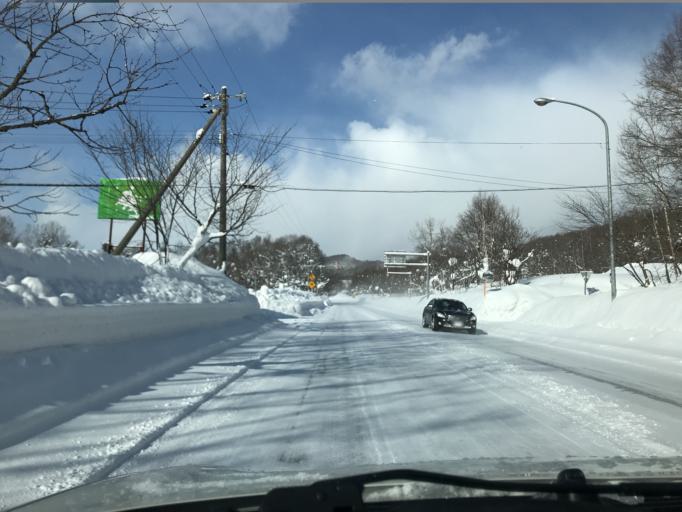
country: JP
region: Hokkaido
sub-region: Asahikawa-shi
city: Asahikawa
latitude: 43.9307
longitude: 142.4722
